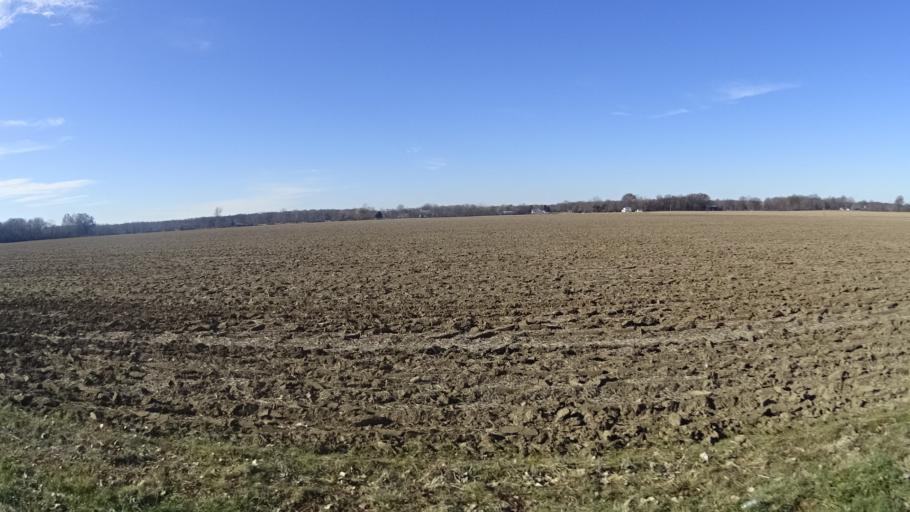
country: US
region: Ohio
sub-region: Lorain County
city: South Amherst
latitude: 41.3126
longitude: -82.2878
